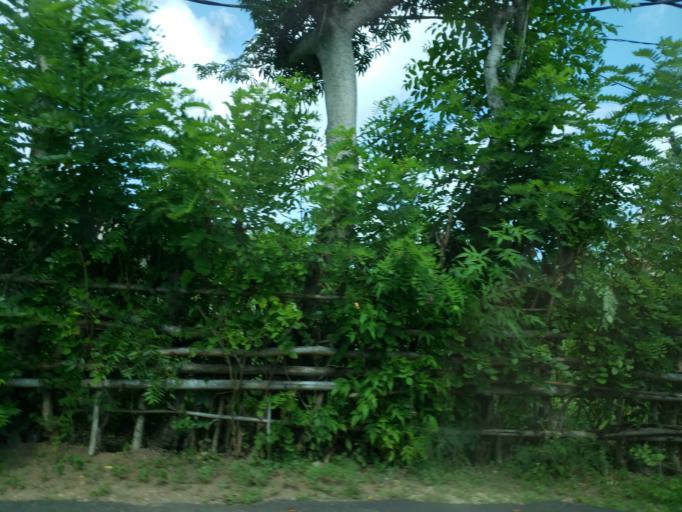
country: ID
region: Bali
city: Pecatu
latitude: -8.8413
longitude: 115.1230
